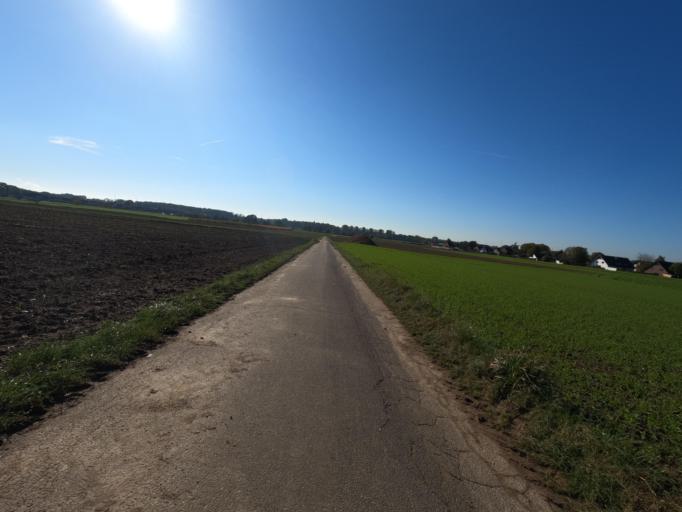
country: DE
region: North Rhine-Westphalia
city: Huckelhoven
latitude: 51.0506
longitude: 6.2383
